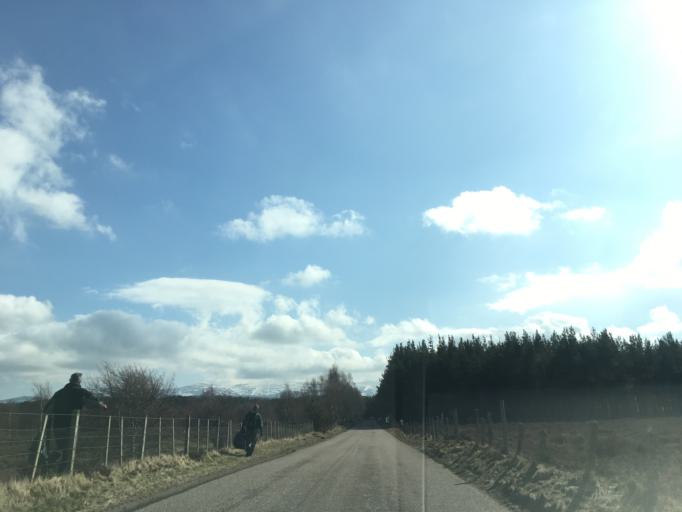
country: GB
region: Scotland
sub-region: Highland
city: Kingussie
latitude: 57.0707
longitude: -4.0103
